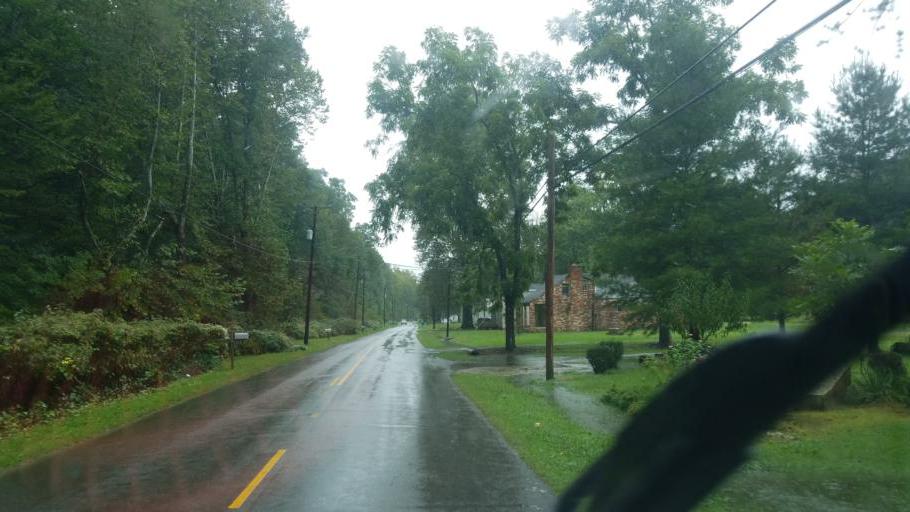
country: US
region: Ohio
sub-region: Scioto County
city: West Portsmouth
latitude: 38.7347
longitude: -83.0643
